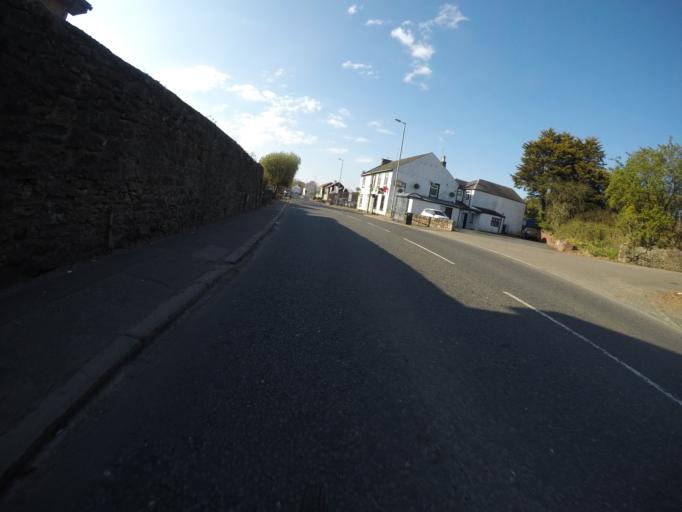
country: GB
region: Scotland
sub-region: North Ayrshire
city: Kilwinning
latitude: 55.6529
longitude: -4.6921
